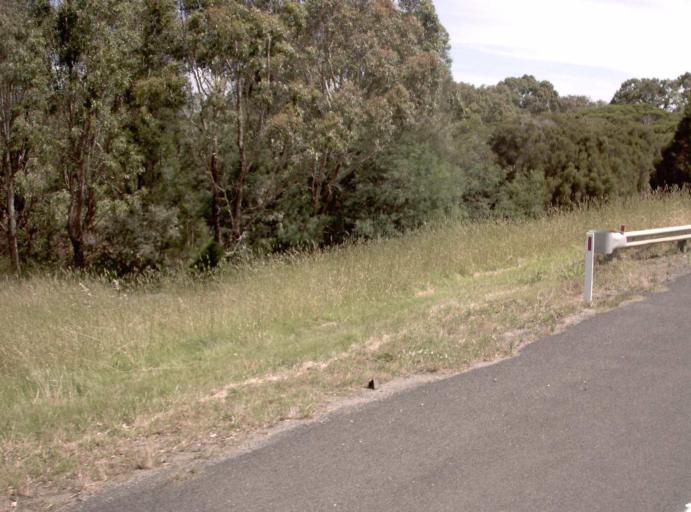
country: AU
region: Victoria
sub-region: Wellington
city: Heyfield
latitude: -38.1534
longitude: 146.7665
